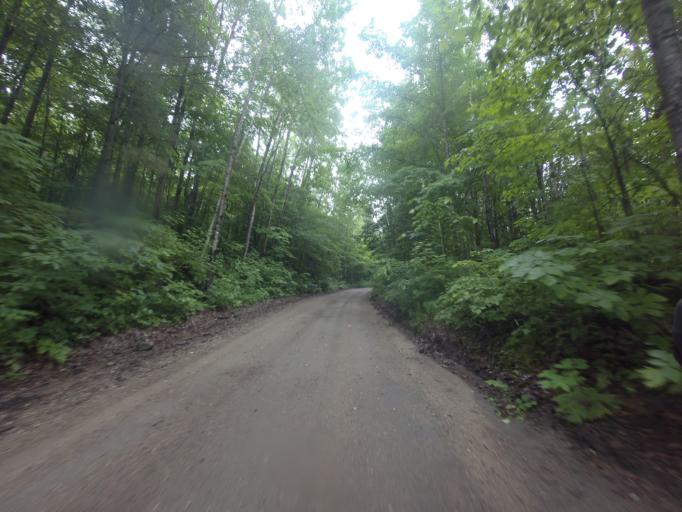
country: CA
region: Quebec
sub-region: Outaouais
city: Maniwaki
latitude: 46.3167
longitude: -76.0072
